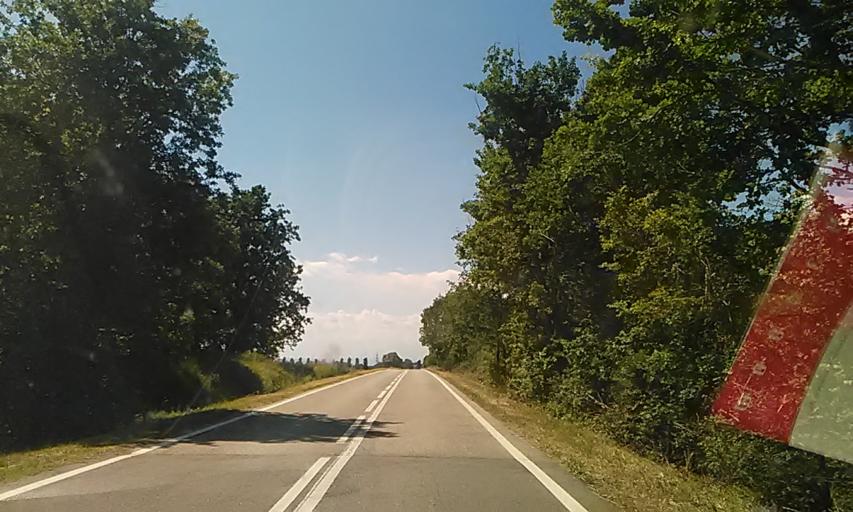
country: IT
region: Piedmont
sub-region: Provincia di Vercelli
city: Villarboit
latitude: 45.4325
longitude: 8.3567
